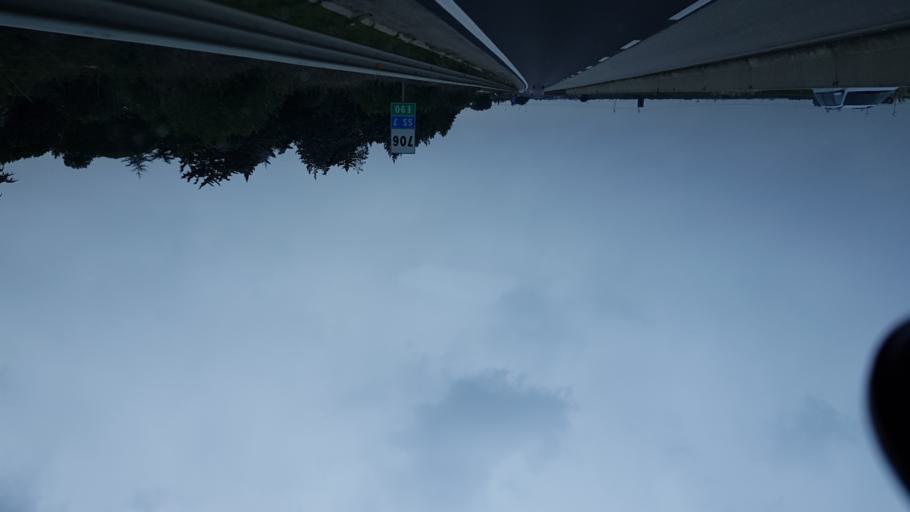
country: IT
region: Apulia
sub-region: Provincia di Brindisi
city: Mesagne
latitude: 40.5858
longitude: 17.8511
